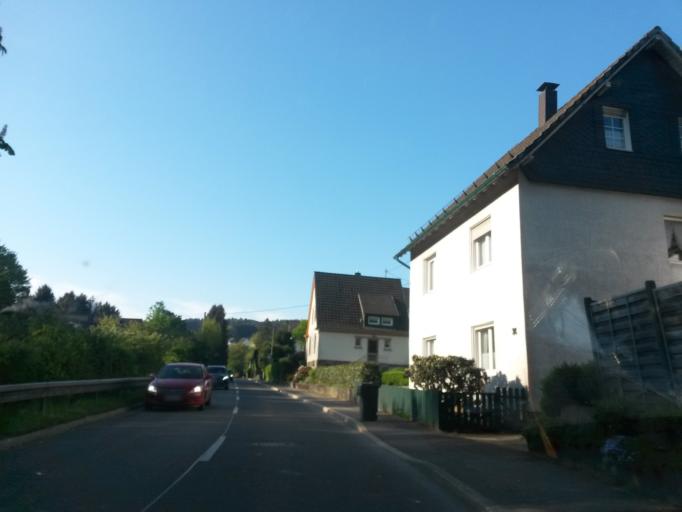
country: DE
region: North Rhine-Westphalia
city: Wiehl
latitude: 50.9595
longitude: 7.5030
